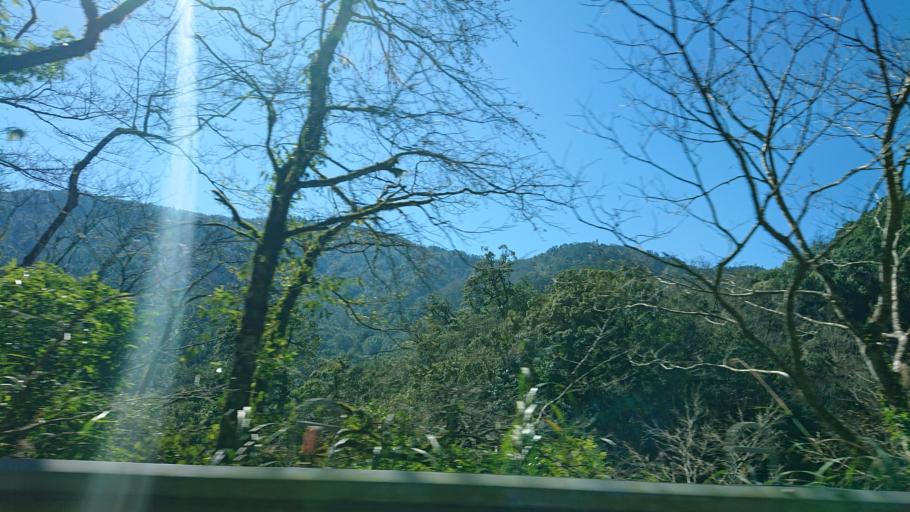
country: TW
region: Taiwan
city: Daxi
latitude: 24.4126
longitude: 121.3614
